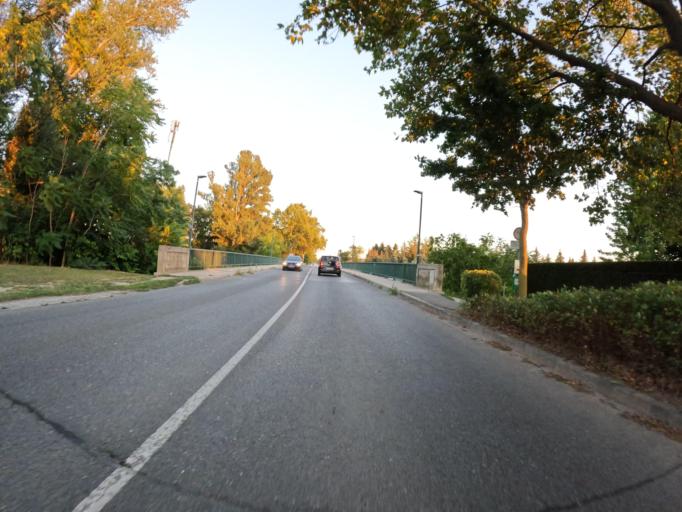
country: AT
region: Lower Austria
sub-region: Politischer Bezirk Baden
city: Pfaffstatten
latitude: 48.0004
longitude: 16.2691
